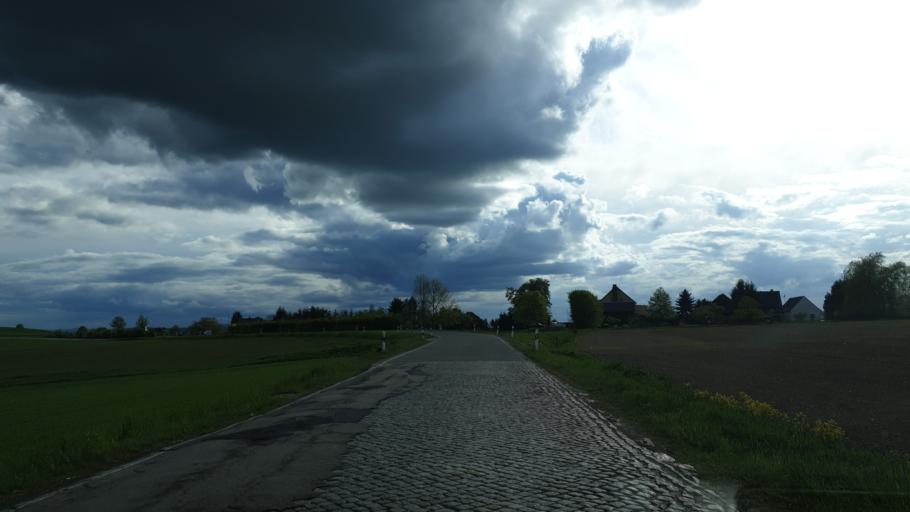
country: DE
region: Saxony
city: Oelsnitz
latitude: 50.6892
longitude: 12.7026
